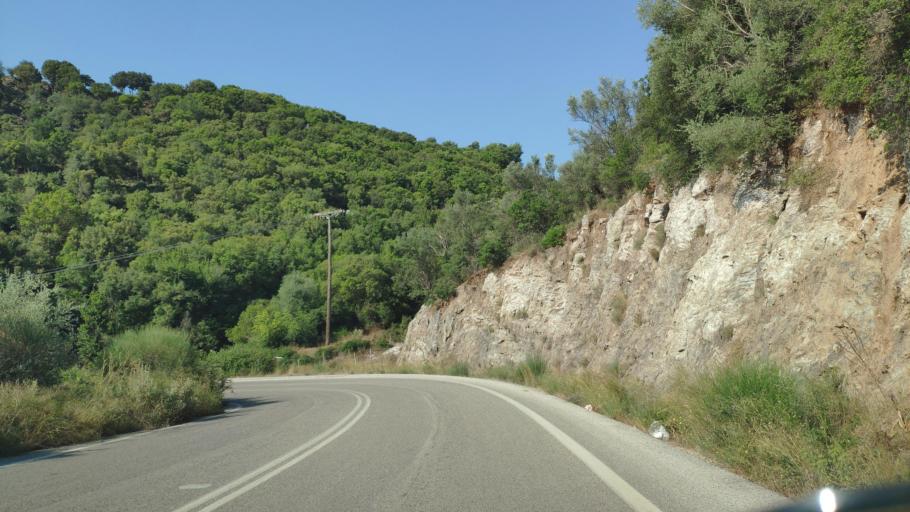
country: GR
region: West Greece
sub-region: Nomos Aitolias kai Akarnanias
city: Katouna
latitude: 38.7802
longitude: 21.1349
